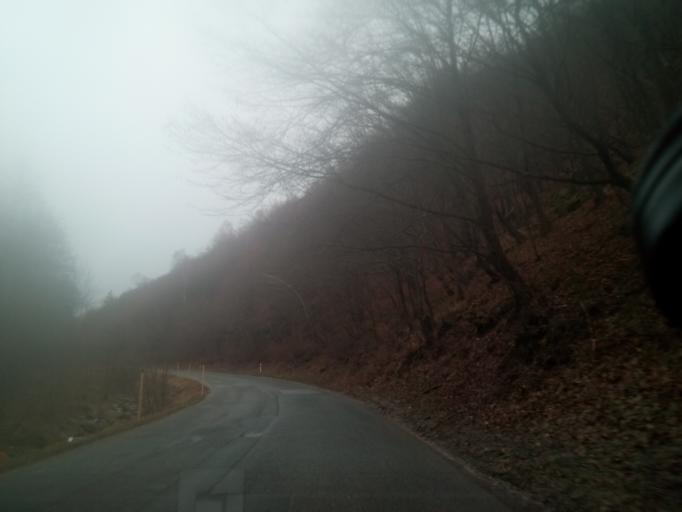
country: SK
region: Kosicky
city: Krompachy
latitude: 48.9471
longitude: 20.9498
